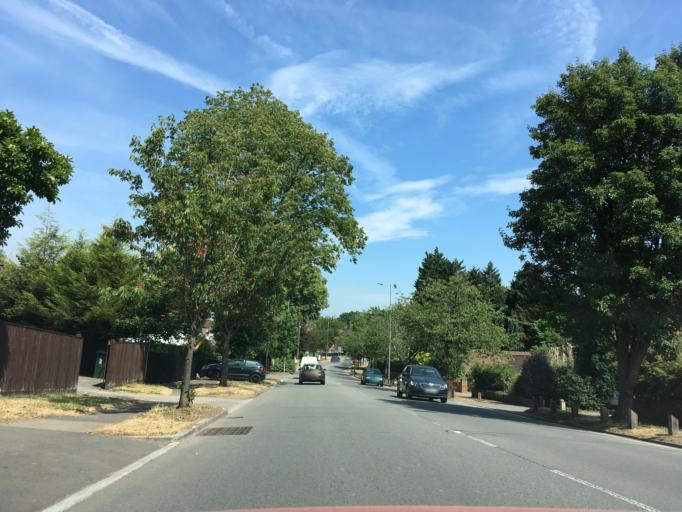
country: GB
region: Wales
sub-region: Newport
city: Newport
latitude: 51.5846
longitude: -3.0221
